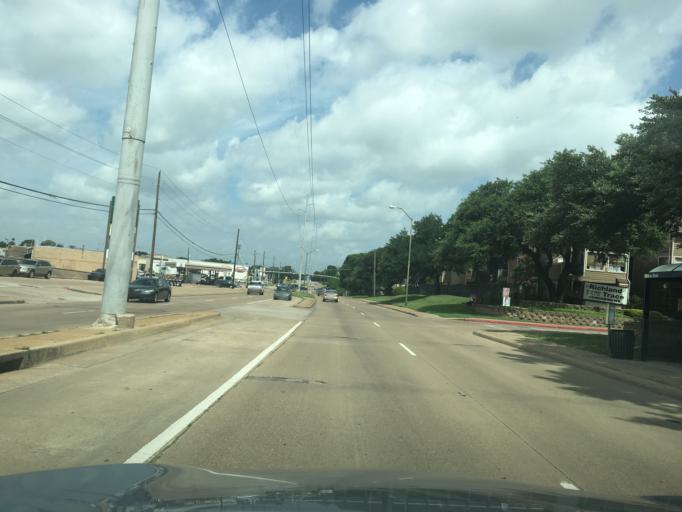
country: US
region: Texas
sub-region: Dallas County
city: Richardson
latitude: 32.9219
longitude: -96.7156
